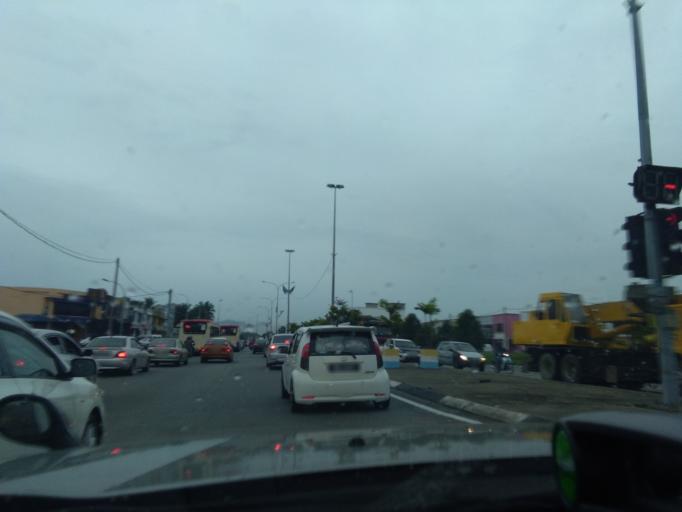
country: MY
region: Penang
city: Nibong Tebal
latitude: 5.1792
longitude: 100.4831
